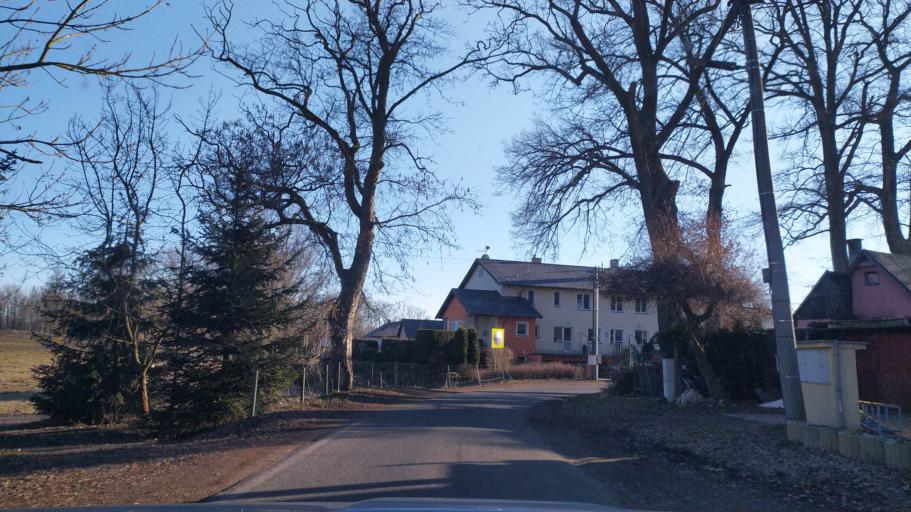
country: CZ
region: Karlovarsky
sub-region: Okres Cheb
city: Frantiskovy Lazne
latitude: 50.0994
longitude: 12.3417
